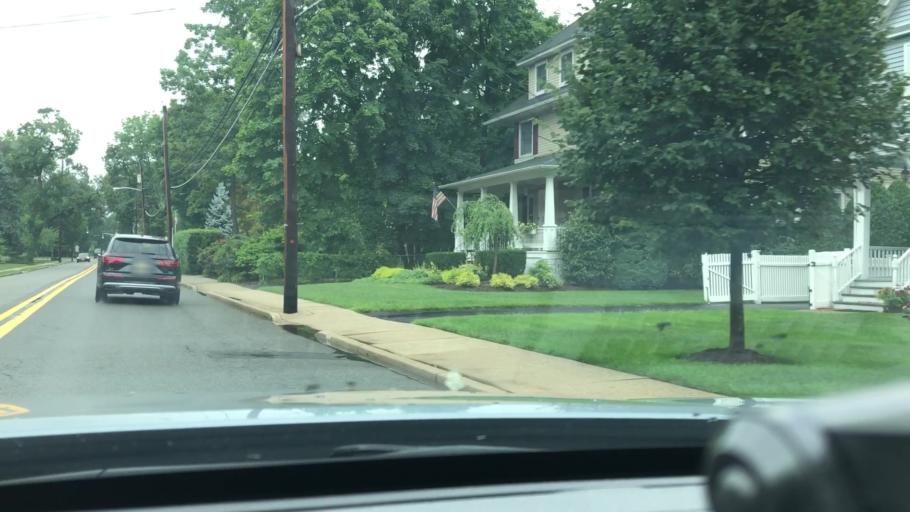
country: US
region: New Jersey
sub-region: Bergen County
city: Ho-Ho-Kus
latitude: 41.0008
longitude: -74.1091
